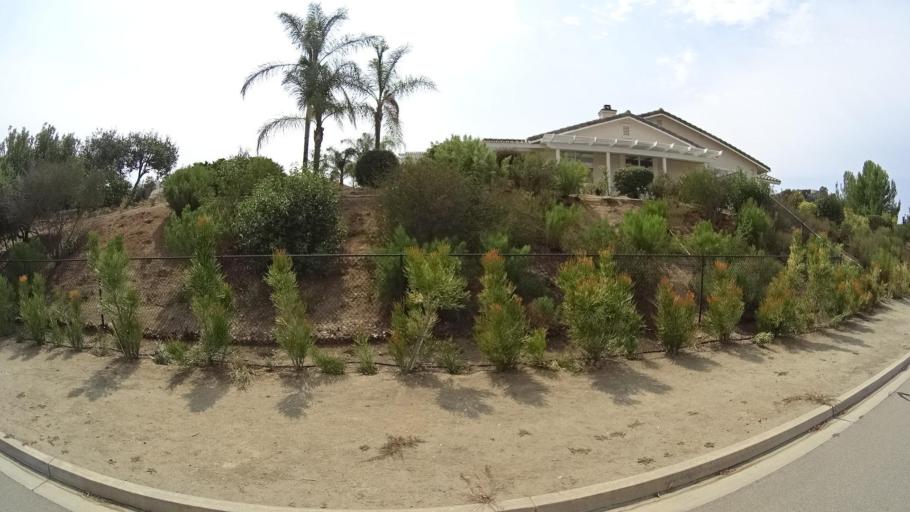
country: US
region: California
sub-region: San Diego County
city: Ramona
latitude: 32.9972
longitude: -116.8959
